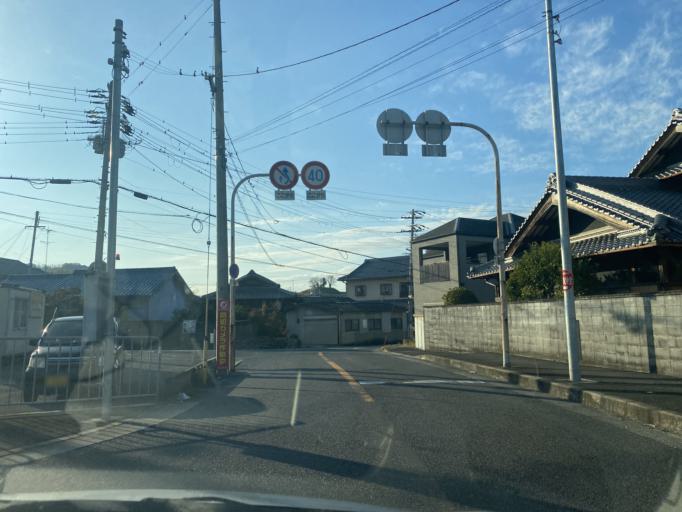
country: JP
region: Osaka
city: Izumi
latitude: 34.4241
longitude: 135.4397
